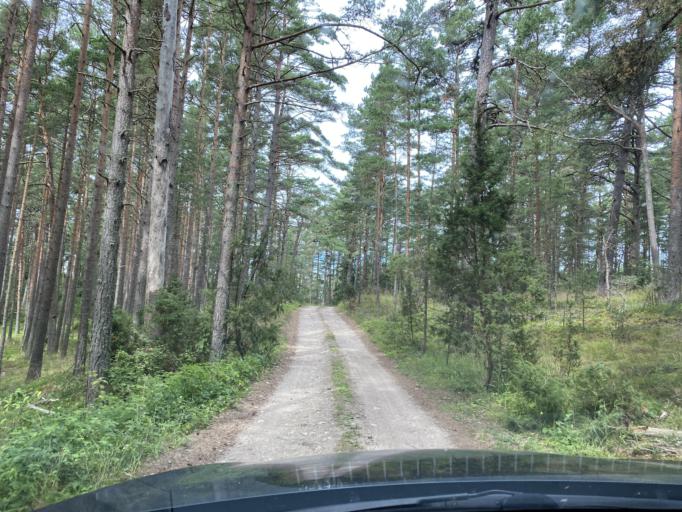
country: LV
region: Ventspils
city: Ventspils
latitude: 57.2089
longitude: 21.4189
